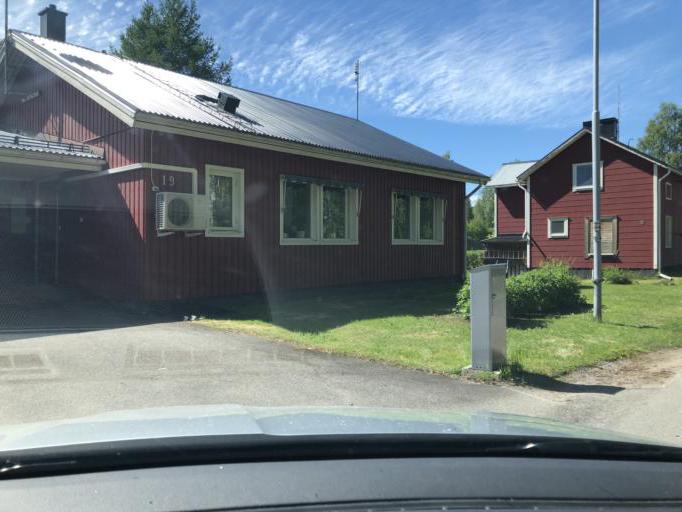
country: SE
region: Norrbotten
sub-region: Alvsbyns Kommun
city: AElvsbyn
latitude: 65.6684
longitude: 21.0160
